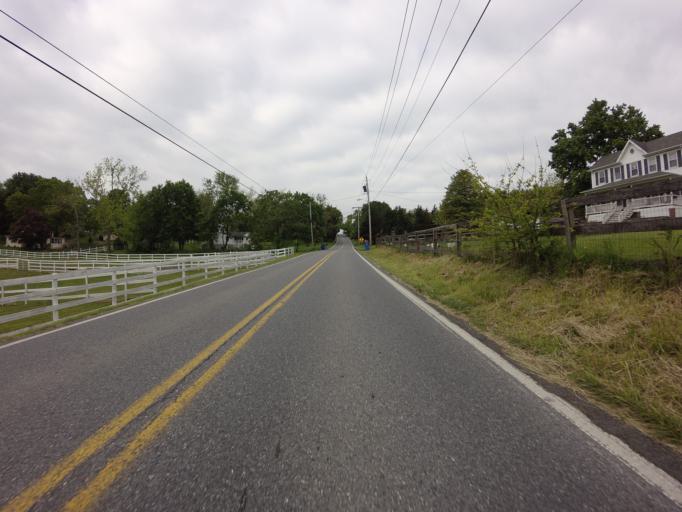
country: US
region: Maryland
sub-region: Frederick County
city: Green Valley
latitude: 39.2964
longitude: -77.2599
